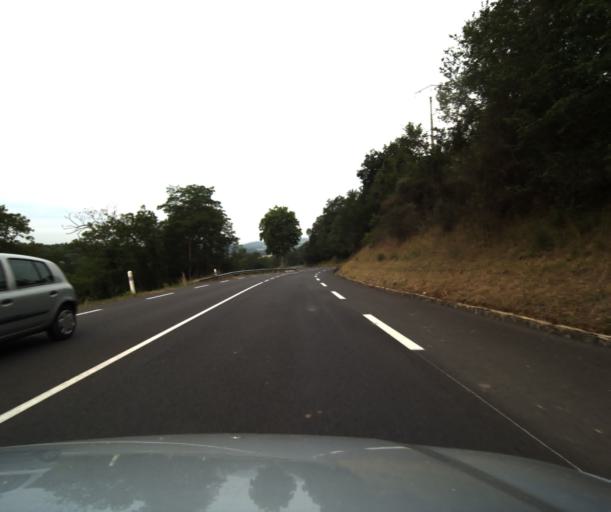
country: FR
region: Midi-Pyrenees
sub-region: Departement du Gers
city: Mielan
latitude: 43.4250
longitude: 0.3038
